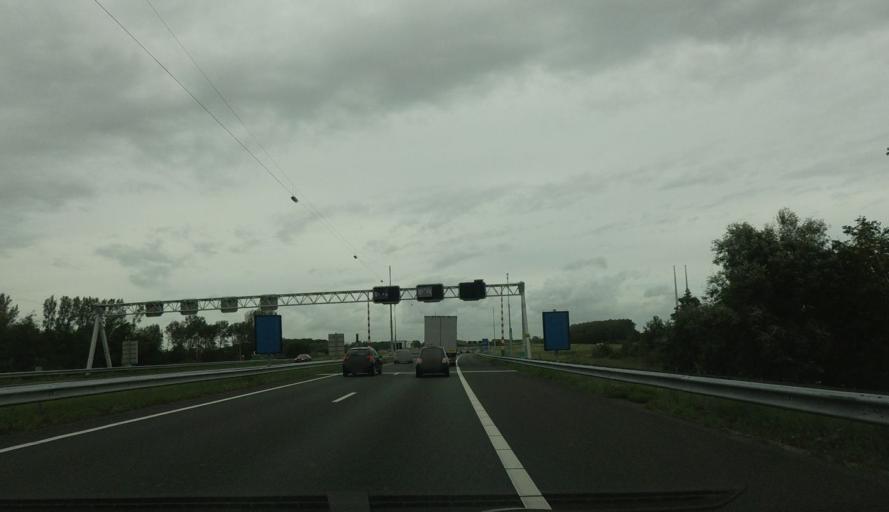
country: NL
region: North Holland
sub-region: Gemeente Velsen
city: Velsen-Zuid
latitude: 52.4494
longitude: 4.6674
